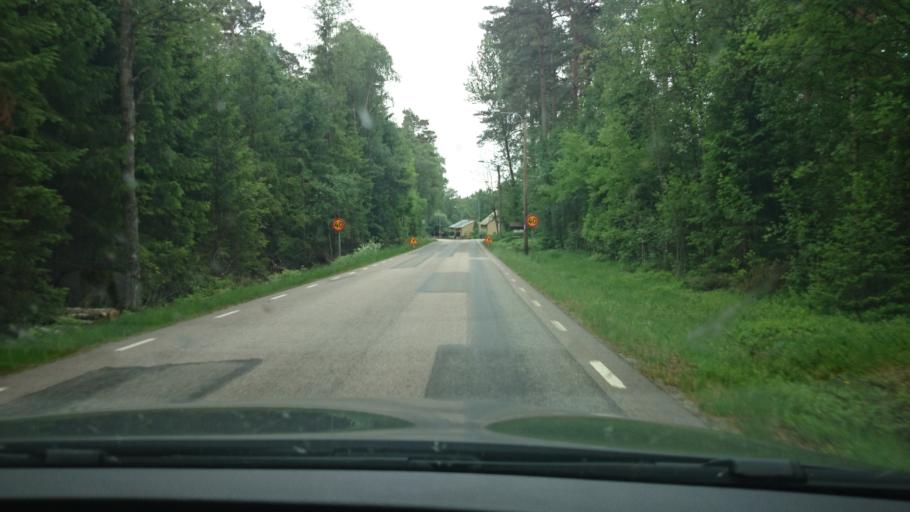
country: SE
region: Halland
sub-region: Hylte Kommun
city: Torup
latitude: 56.9665
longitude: 13.1437
